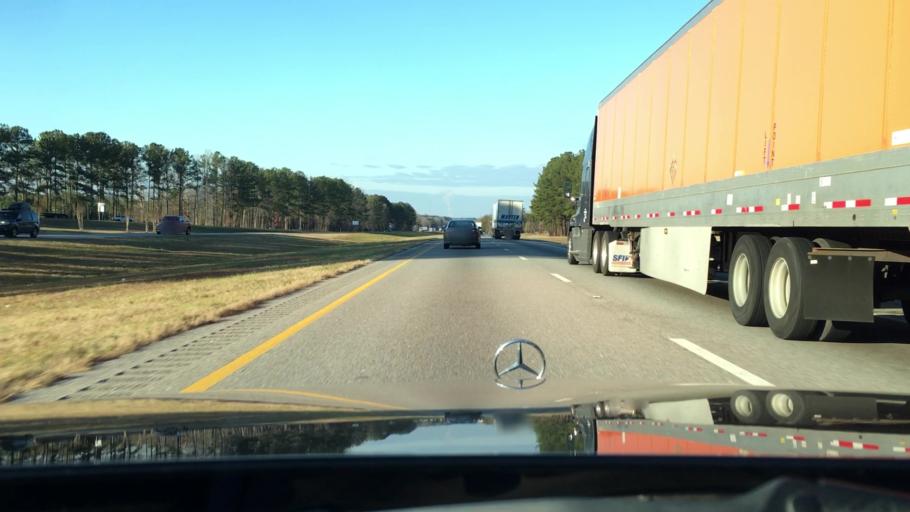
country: US
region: South Carolina
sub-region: Chester County
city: Eureka Mill
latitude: 34.7462
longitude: -81.0354
